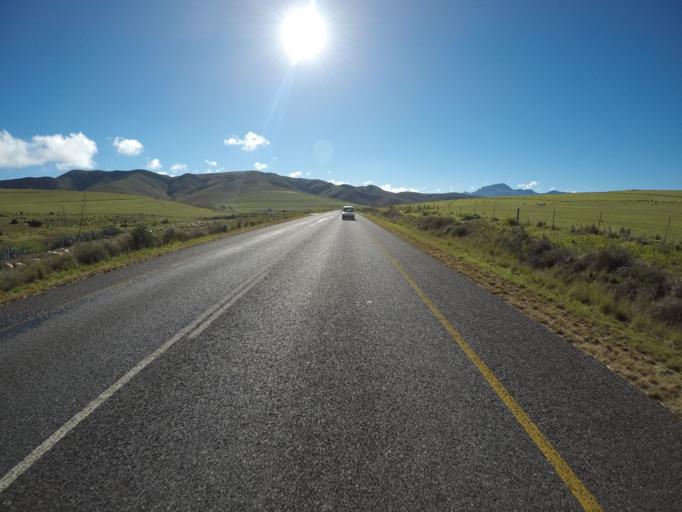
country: ZA
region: Western Cape
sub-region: Overberg District Municipality
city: Caledon
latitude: -34.1073
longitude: 19.5258
